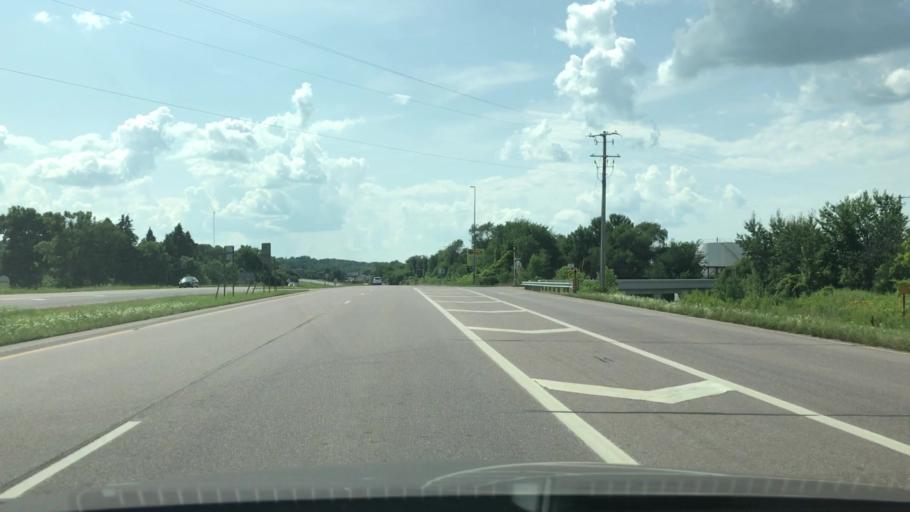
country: US
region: Minnesota
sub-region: Nicollet County
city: North Mankato
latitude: 44.1525
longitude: -94.0620
